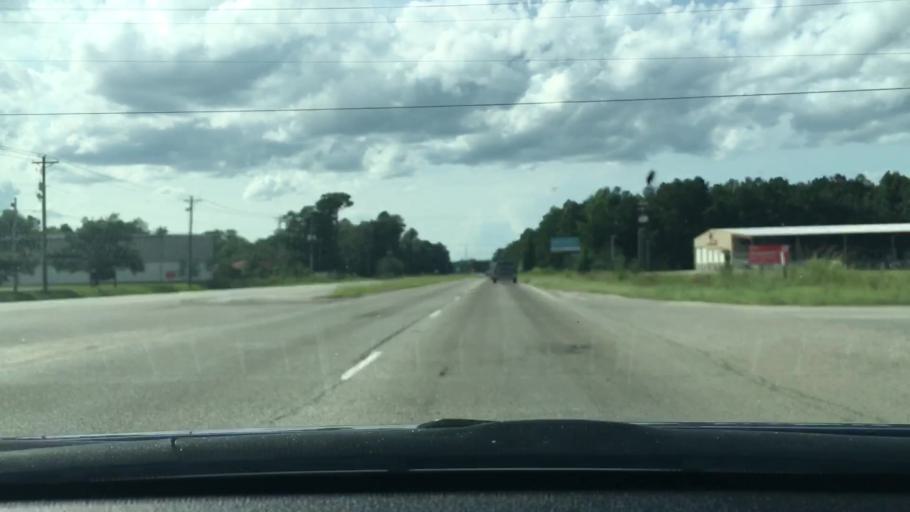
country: US
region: South Carolina
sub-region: Richland County
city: Forest Acres
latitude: 33.9444
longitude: -80.9614
